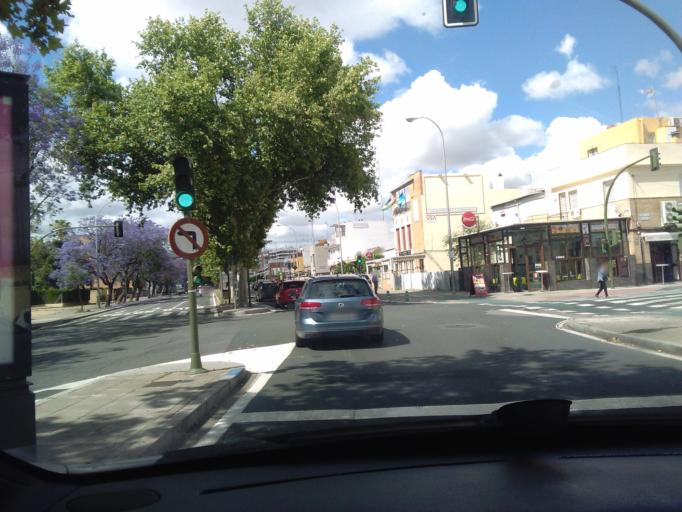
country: ES
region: Andalusia
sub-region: Provincia de Sevilla
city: Sevilla
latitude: 37.3771
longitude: -5.9664
